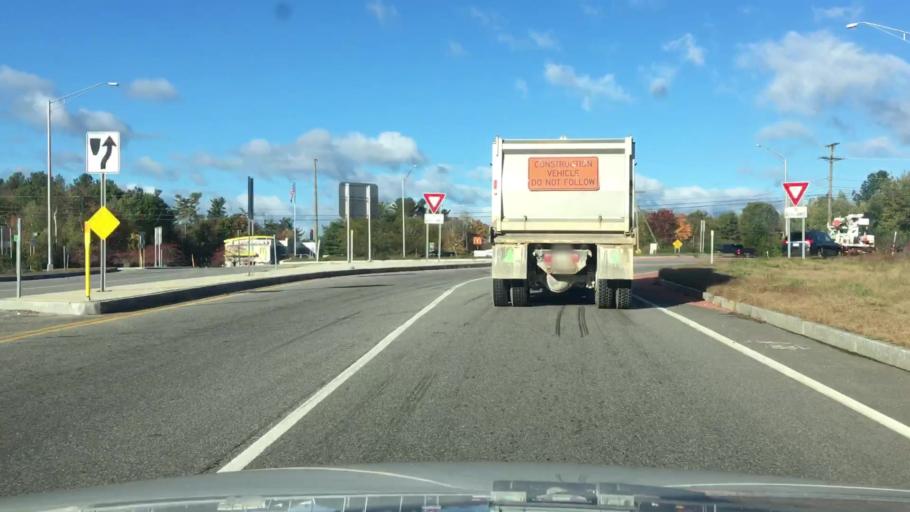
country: US
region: New Hampshire
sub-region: Strafford County
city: Lee
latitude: 43.1491
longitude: -71.0058
